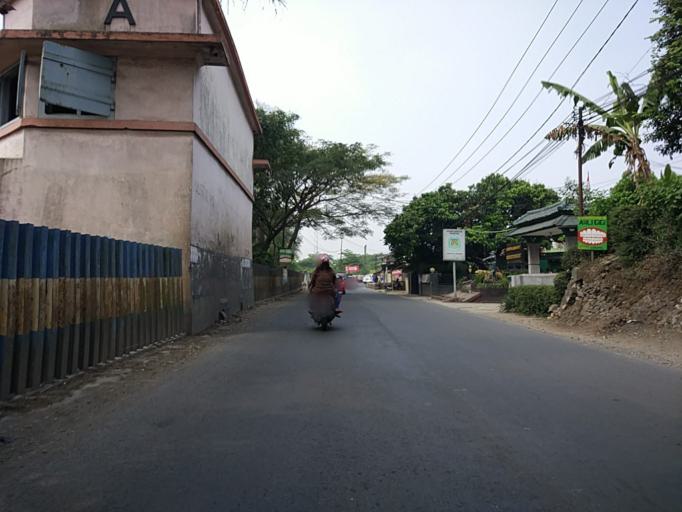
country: ID
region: West Java
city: Padalarang
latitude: -6.8410
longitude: 107.4951
